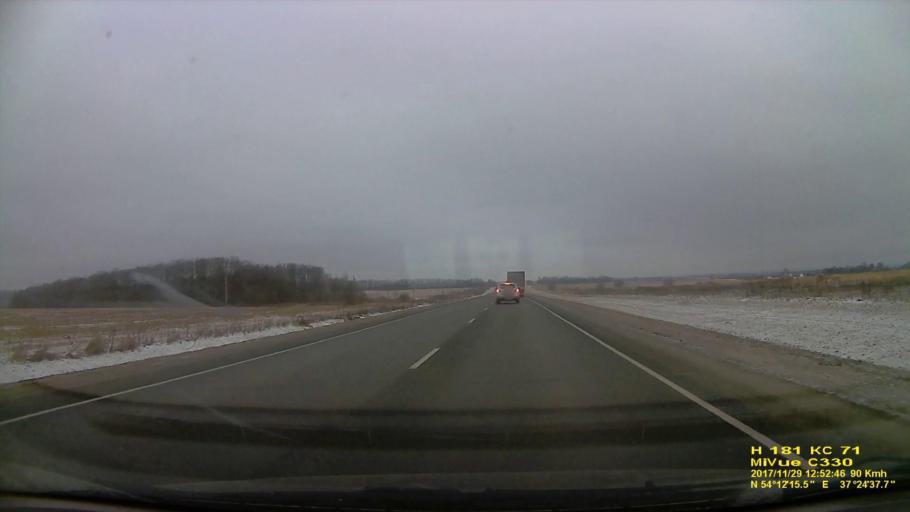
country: RU
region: Tula
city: Leninskiy
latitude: 54.2044
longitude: 37.4103
